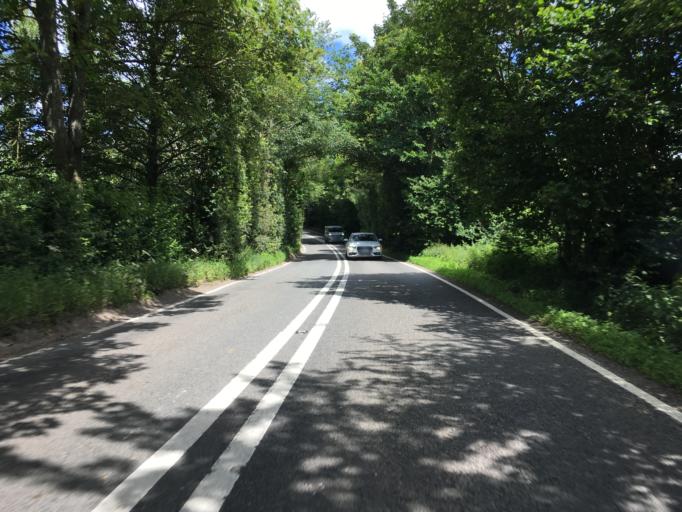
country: GB
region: England
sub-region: Hampshire
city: Highclere
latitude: 51.3289
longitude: -1.3795
